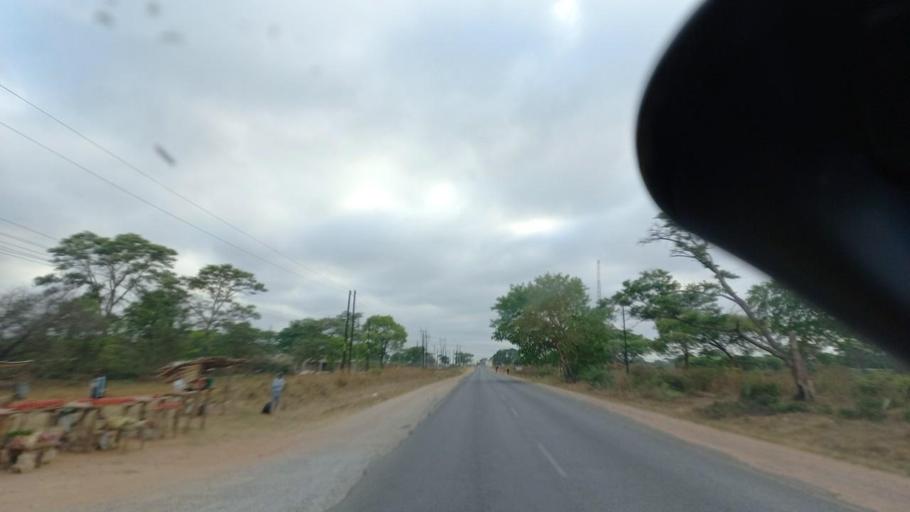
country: ZM
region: Lusaka
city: Chongwe
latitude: -15.3447
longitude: 28.5114
